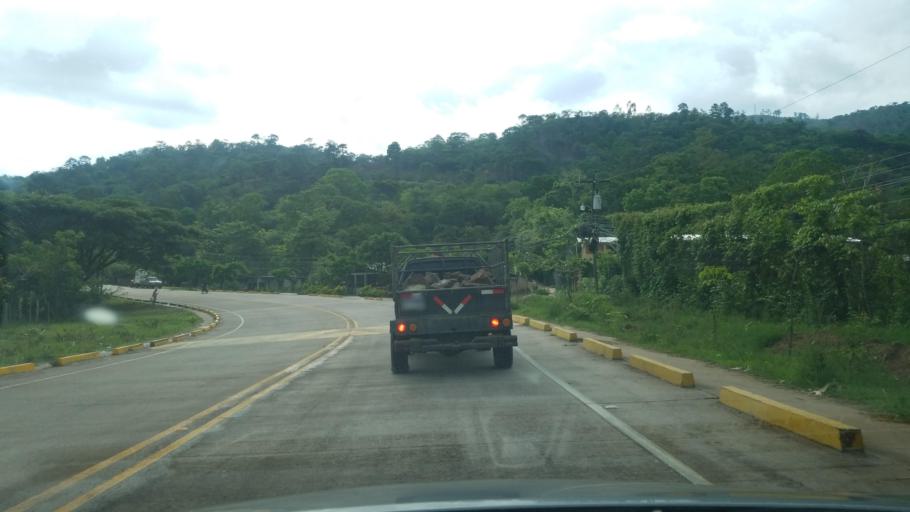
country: HN
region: Copan
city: Copan
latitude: 14.8423
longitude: -89.1700
